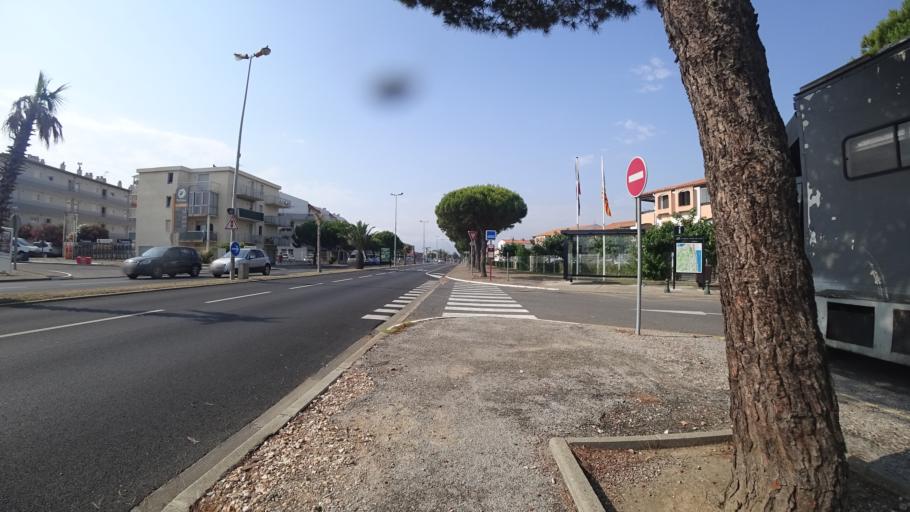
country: FR
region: Languedoc-Roussillon
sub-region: Departement des Pyrenees-Orientales
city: Saint-Cyprien-Plage
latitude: 42.6359
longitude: 3.0334
